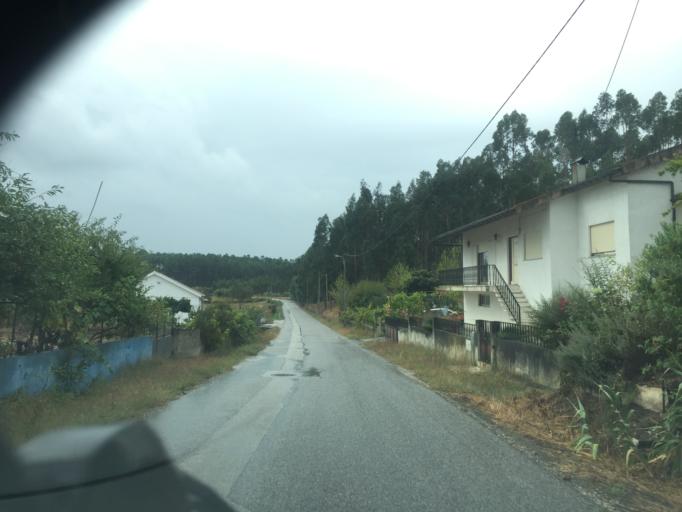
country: PT
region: Leiria
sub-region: Pombal
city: Lourical
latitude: 40.0585
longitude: -8.7717
